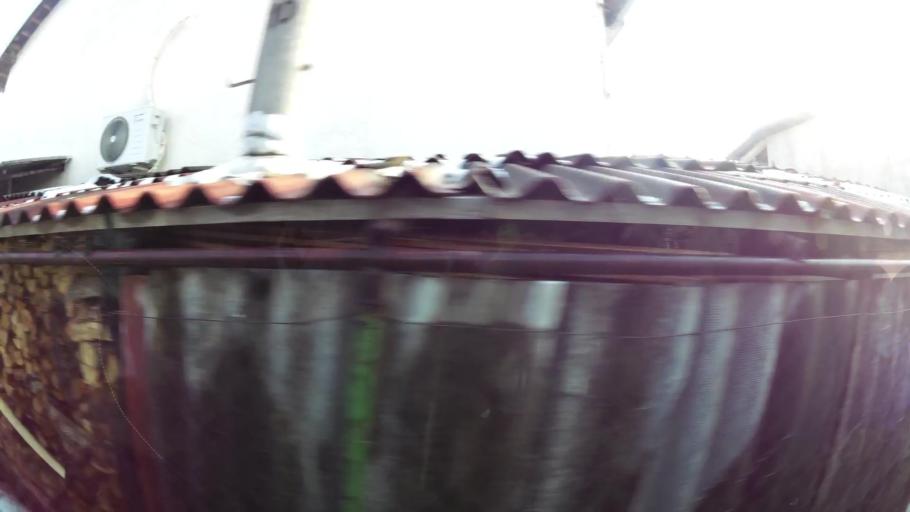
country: MK
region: Ilinden
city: Marino
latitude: 41.9844
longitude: 21.5919
